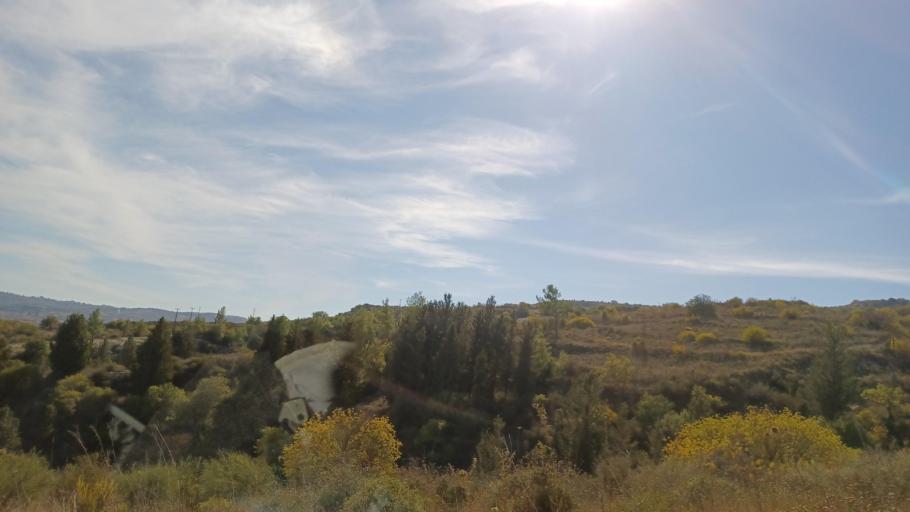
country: CY
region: Pafos
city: Pegeia
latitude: 34.9382
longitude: 32.4544
